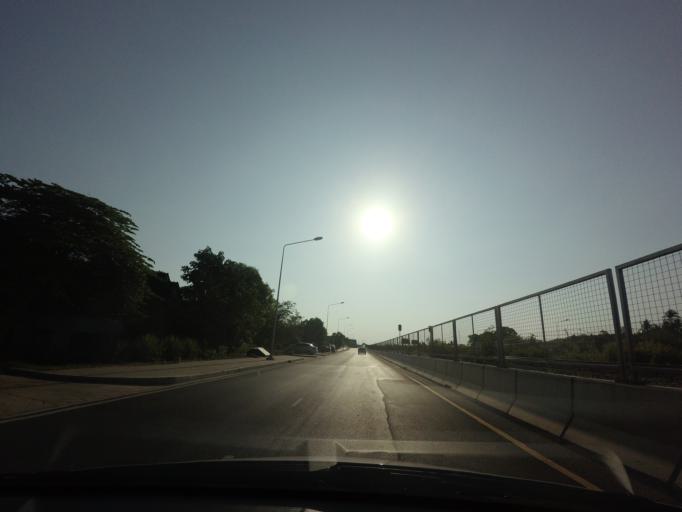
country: TH
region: Bangkok
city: Taling Chan
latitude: 13.7991
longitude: 100.4177
